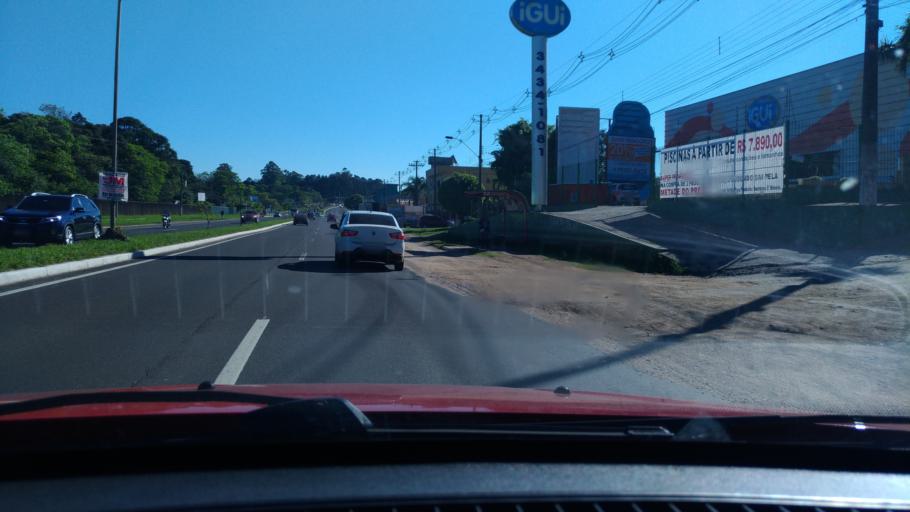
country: BR
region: Rio Grande do Sul
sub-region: Viamao
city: Viamao
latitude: -30.0815
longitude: -51.0524
